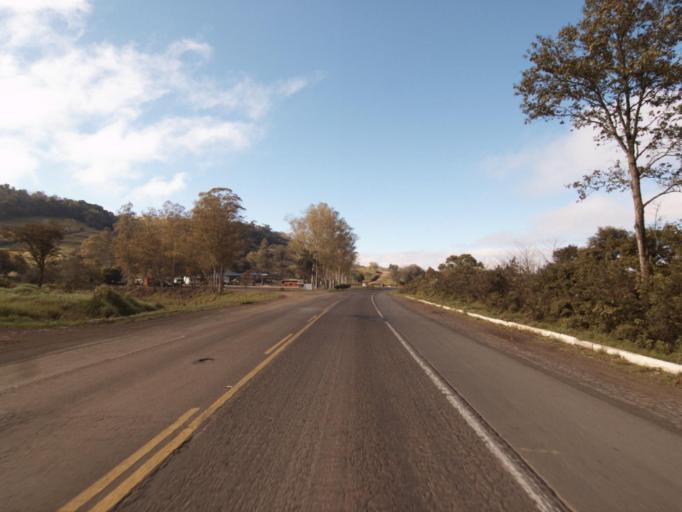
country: BR
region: Rio Grande do Sul
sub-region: Frederico Westphalen
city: Frederico Westphalen
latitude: -27.0358
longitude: -53.2312
